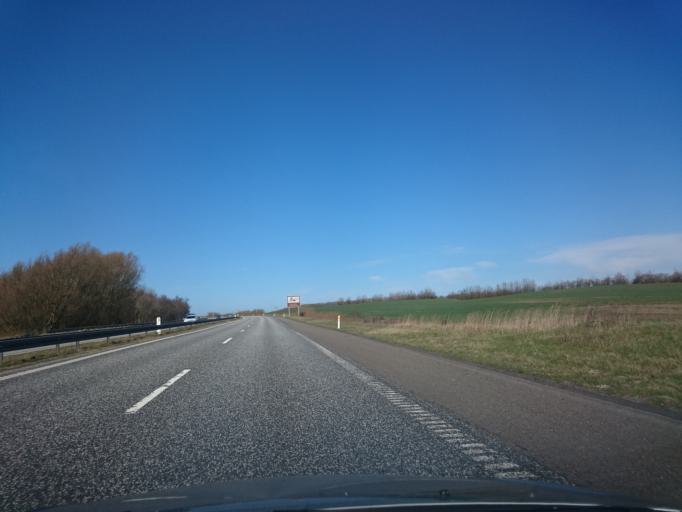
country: DK
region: North Denmark
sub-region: Hjorring Kommune
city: Hirtshals
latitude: 57.5572
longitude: 10.0134
